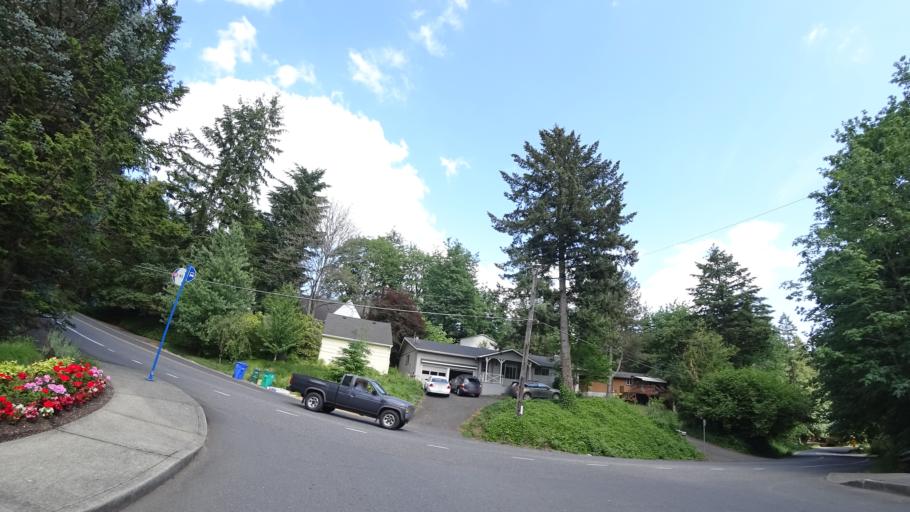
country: US
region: Oregon
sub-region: Washington County
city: Garden Home-Whitford
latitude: 45.4647
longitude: -122.7267
